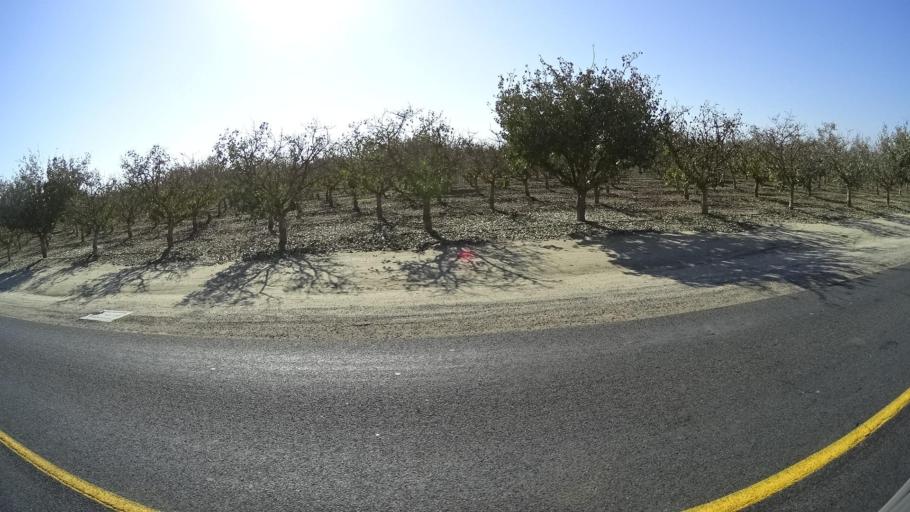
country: US
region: California
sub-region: Kern County
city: Delano
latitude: 35.7177
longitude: -119.3326
